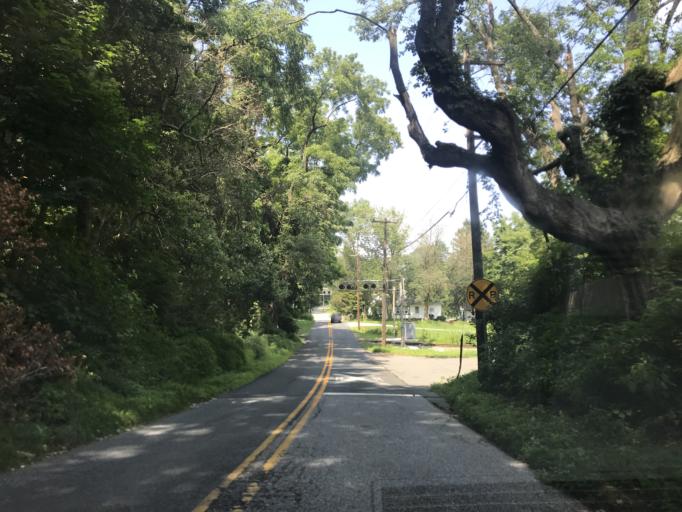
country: US
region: Delaware
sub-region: New Castle County
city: Greenville
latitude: 39.8320
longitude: -75.5861
